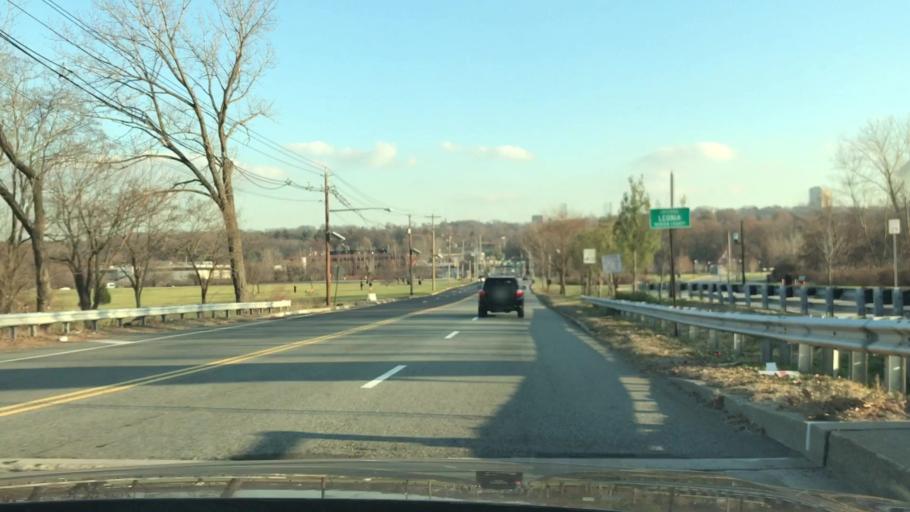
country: US
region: New Jersey
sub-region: Bergen County
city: Leonia
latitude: 40.8666
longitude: -73.9988
